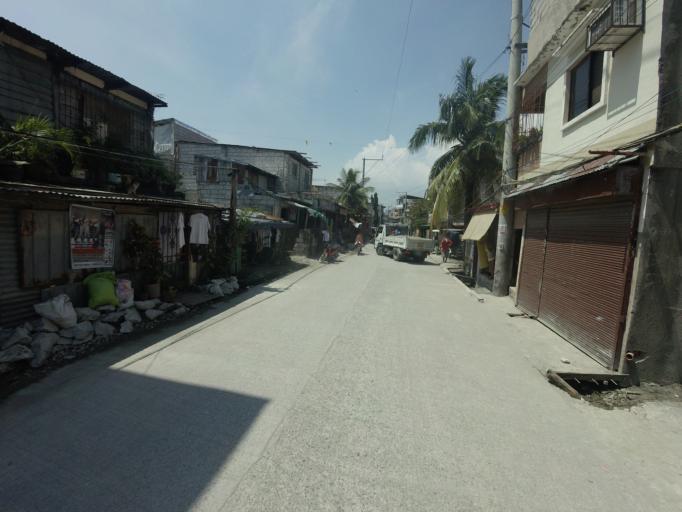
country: PH
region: Calabarzon
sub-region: Province of Rizal
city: Taguig
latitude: 14.5391
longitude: 121.1065
